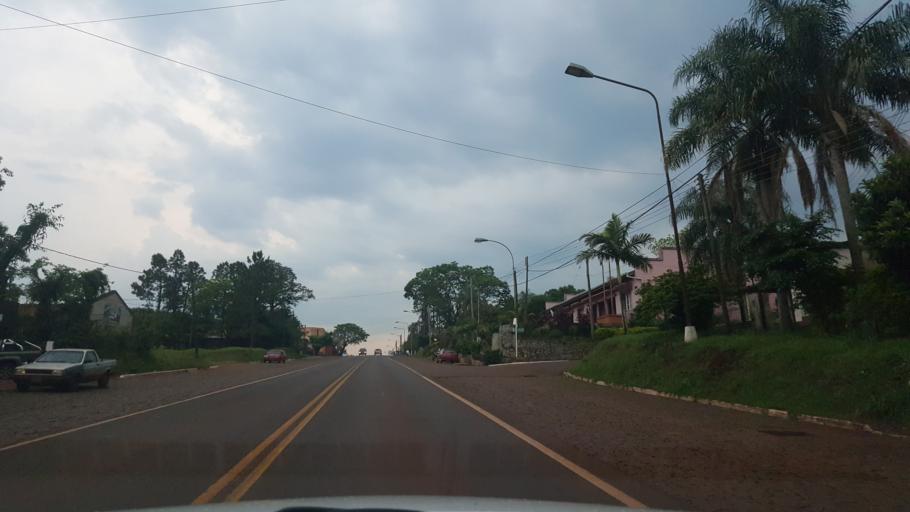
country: AR
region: Misiones
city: Gobernador Roca
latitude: -27.1932
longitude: -55.4720
